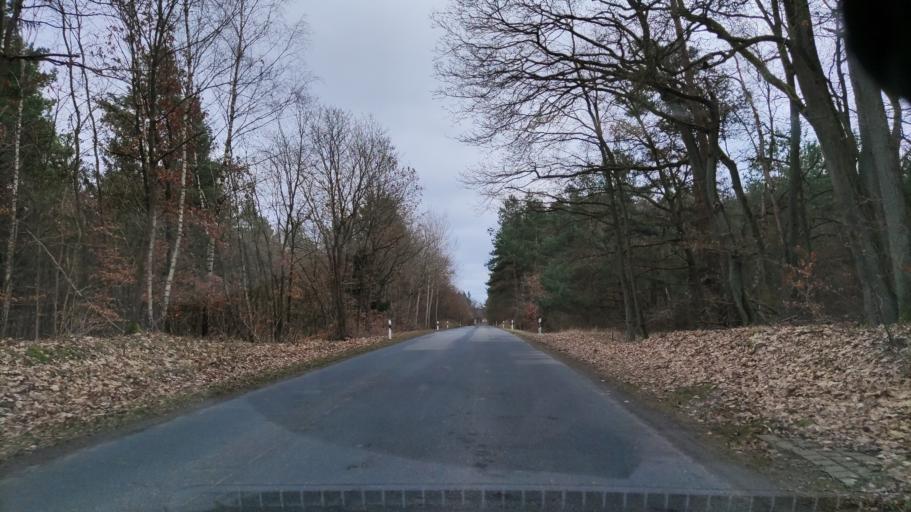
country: DE
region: Lower Saxony
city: Bleckede
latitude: 53.2662
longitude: 10.7220
